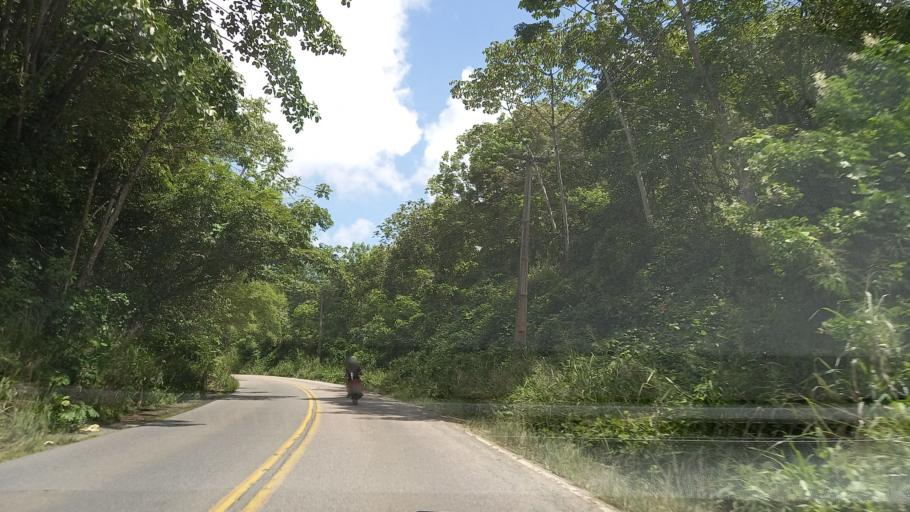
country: BR
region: Pernambuco
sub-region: Rio Formoso
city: Rio Formoso
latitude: -8.6485
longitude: -35.1305
